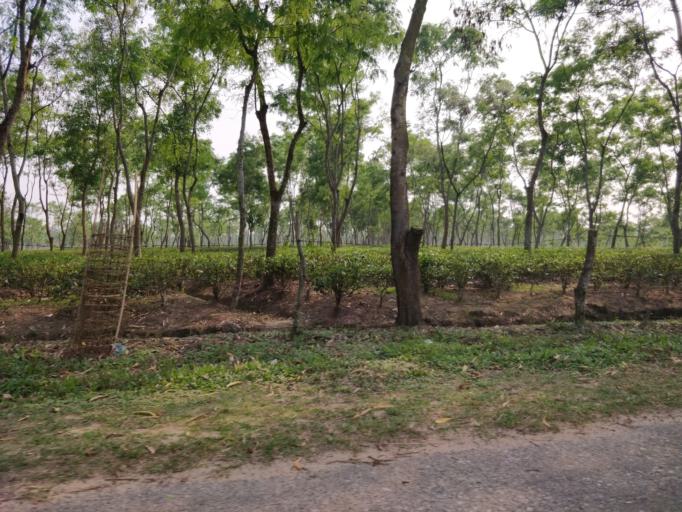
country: IN
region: Tripura
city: Khowai
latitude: 24.1296
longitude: 91.3882
